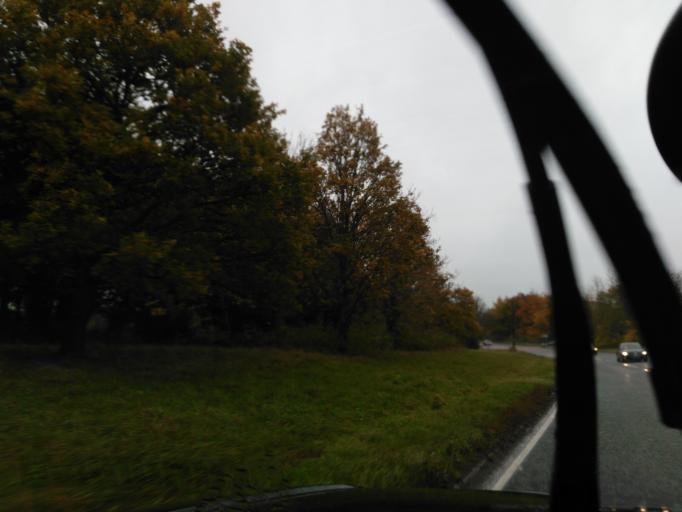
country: GB
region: England
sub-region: Bath and North East Somerset
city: Freshford
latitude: 51.3385
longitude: -2.3196
